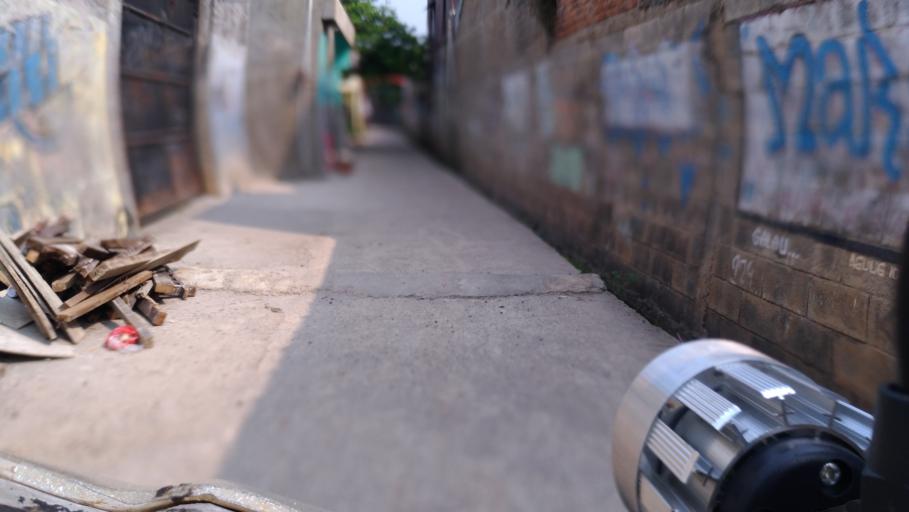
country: ID
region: West Java
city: Depok
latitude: -6.3680
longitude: 106.8764
